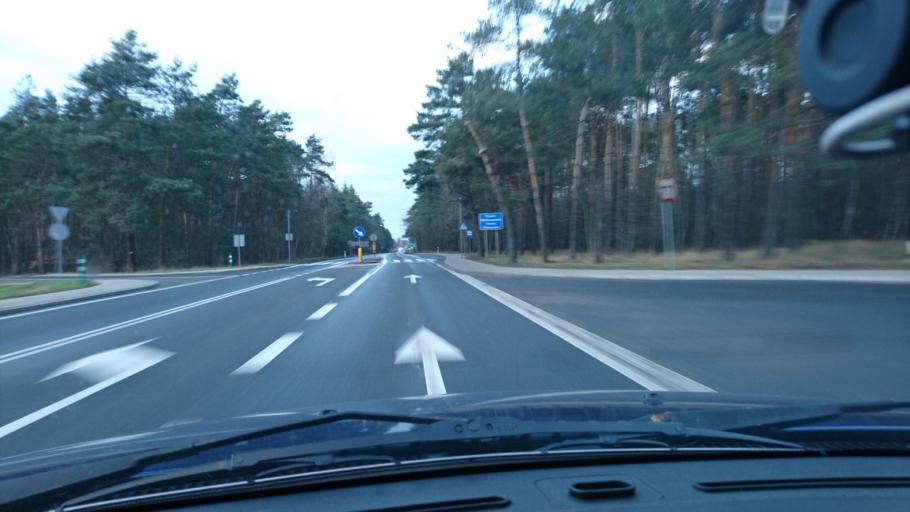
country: PL
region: Greater Poland Voivodeship
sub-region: Powiat kepinski
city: Kepno
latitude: 51.3412
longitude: 17.9525
